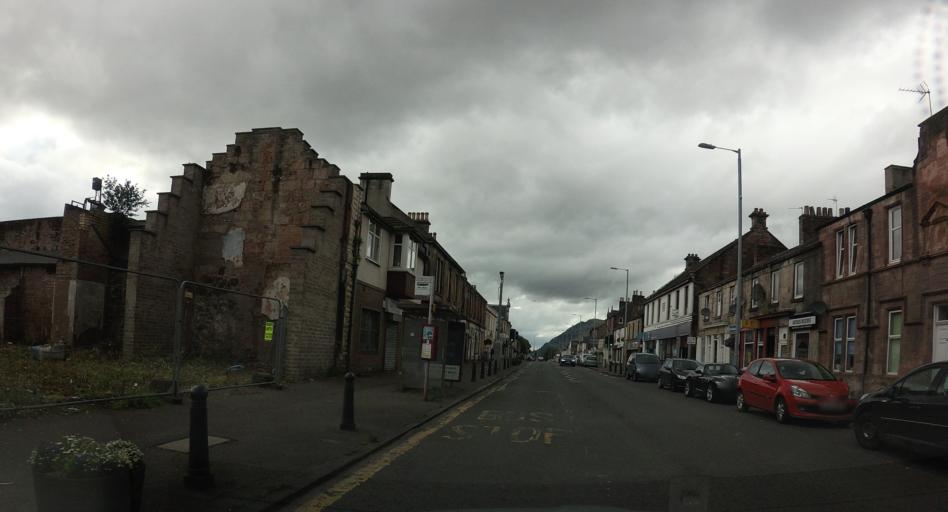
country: GB
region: Scotland
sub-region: Clackmannanshire
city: Alva
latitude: 56.1531
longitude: -3.7990
